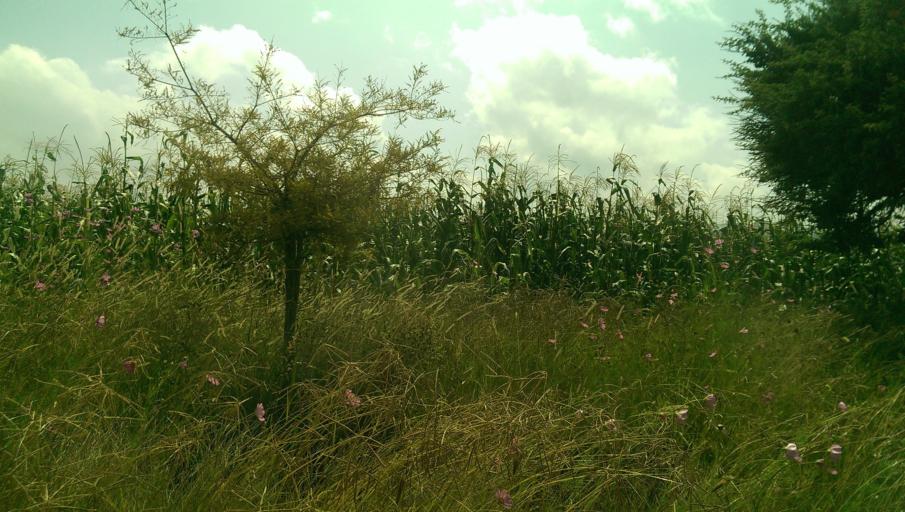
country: MX
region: Queretaro
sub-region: Huimilpan
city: San Jose Tepuzas
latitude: 20.3561
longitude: -100.3924
